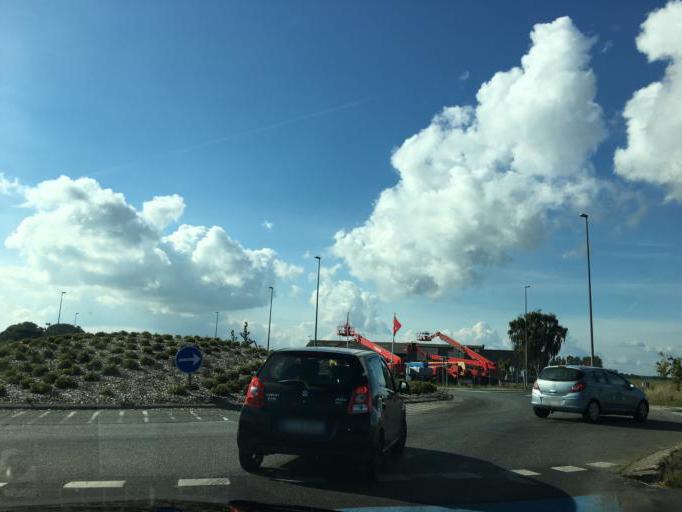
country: DK
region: South Denmark
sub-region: Fredericia Kommune
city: Snoghoj
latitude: 55.5678
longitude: 9.6907
